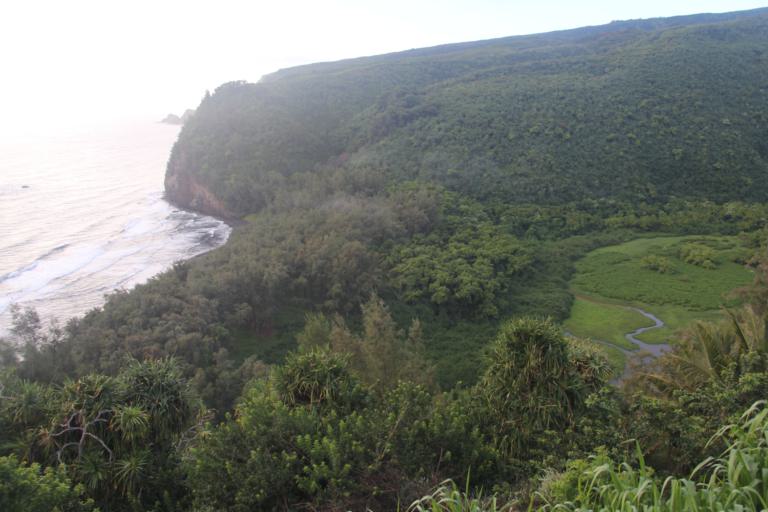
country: US
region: Hawaii
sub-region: Hawaii County
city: Kapaau
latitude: 20.2036
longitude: -155.7338
